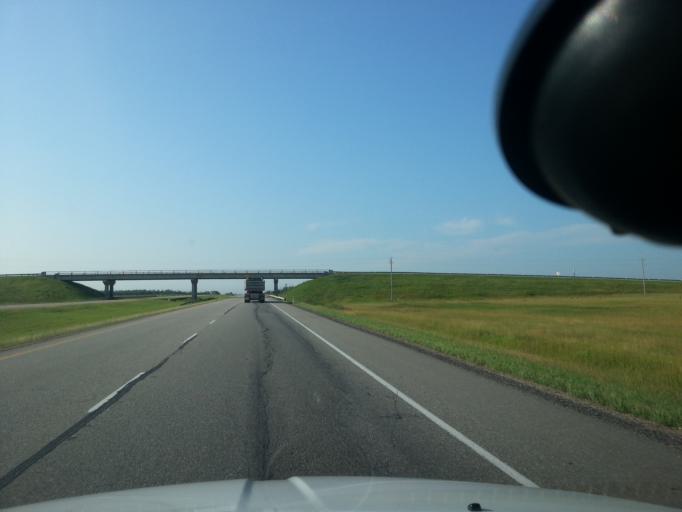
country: CA
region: Alberta
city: Millet
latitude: 53.0923
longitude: -113.5984
